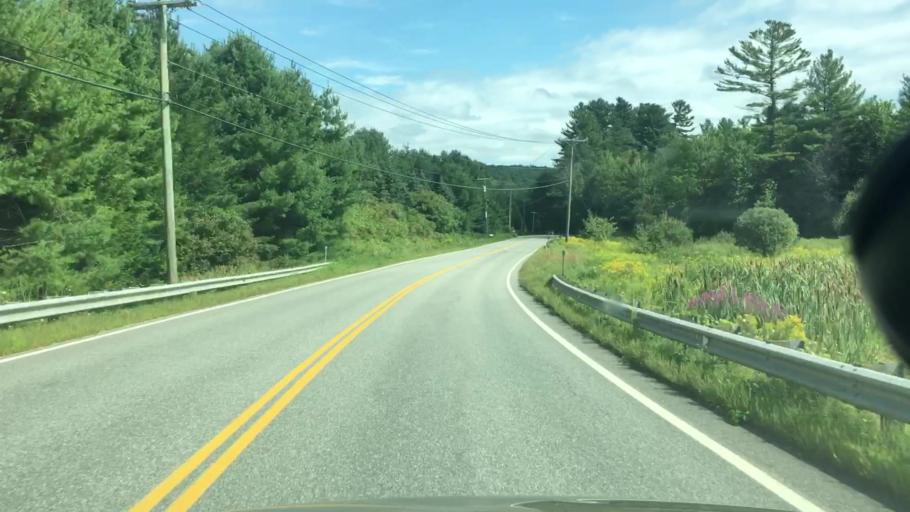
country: US
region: Massachusetts
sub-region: Franklin County
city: Shelburne
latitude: 42.6301
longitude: -72.6692
